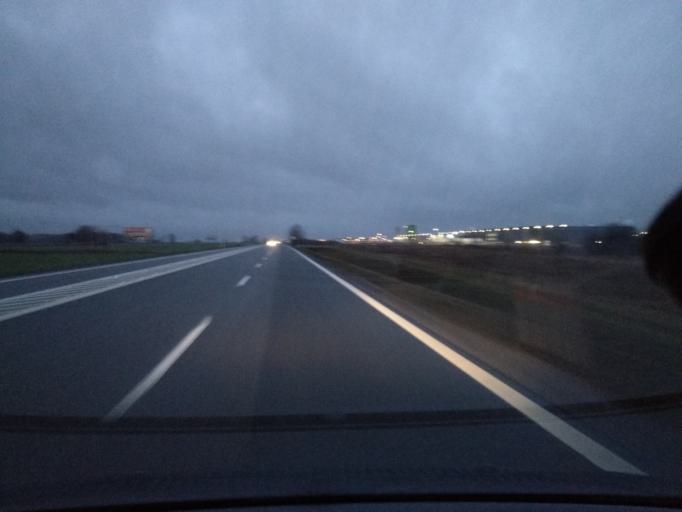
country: PL
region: Lower Silesian Voivodeship
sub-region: Powiat sredzki
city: Miekinia
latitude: 51.1628
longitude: 16.6740
